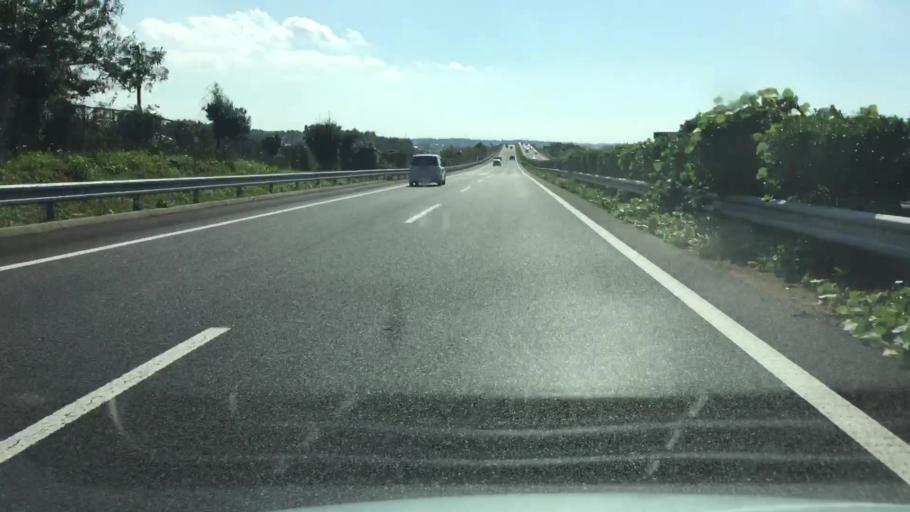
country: JP
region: Ibaraki
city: Tomobe
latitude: 36.3331
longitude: 140.2882
